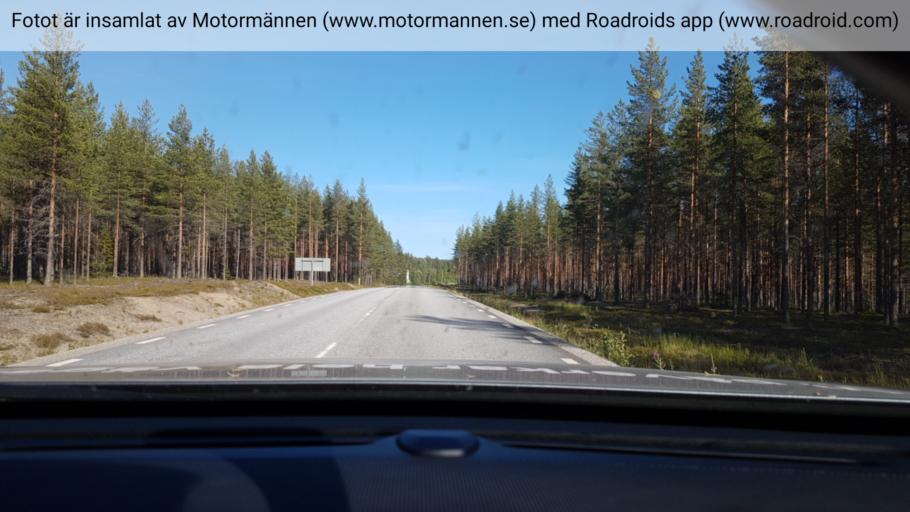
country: SE
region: Vaesterbotten
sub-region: Vindelns Kommun
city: Vindeln
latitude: 64.2031
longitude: 19.4388
